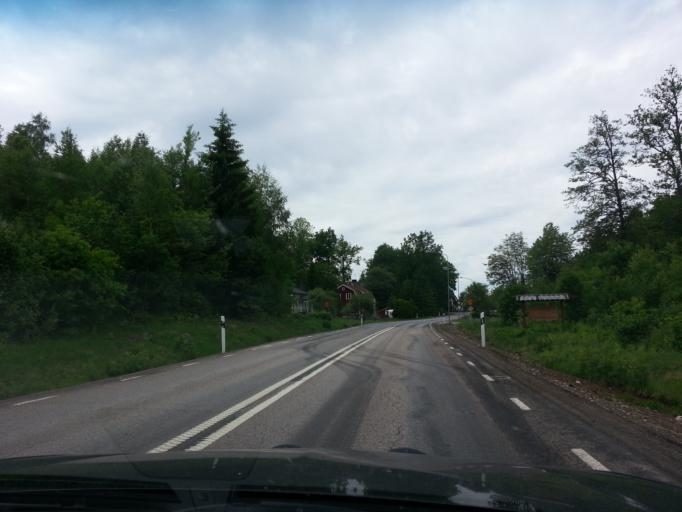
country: SE
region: Joenkoeping
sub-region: Vetlanda Kommun
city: Vetlanda
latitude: 57.2914
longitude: 15.1298
